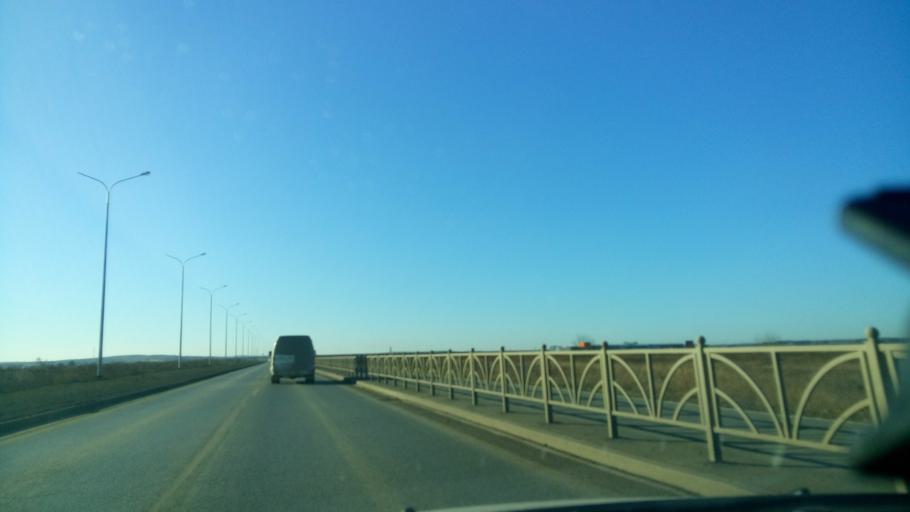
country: RU
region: Sverdlovsk
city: Sovkhoznyy
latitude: 56.7410
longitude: 60.5606
